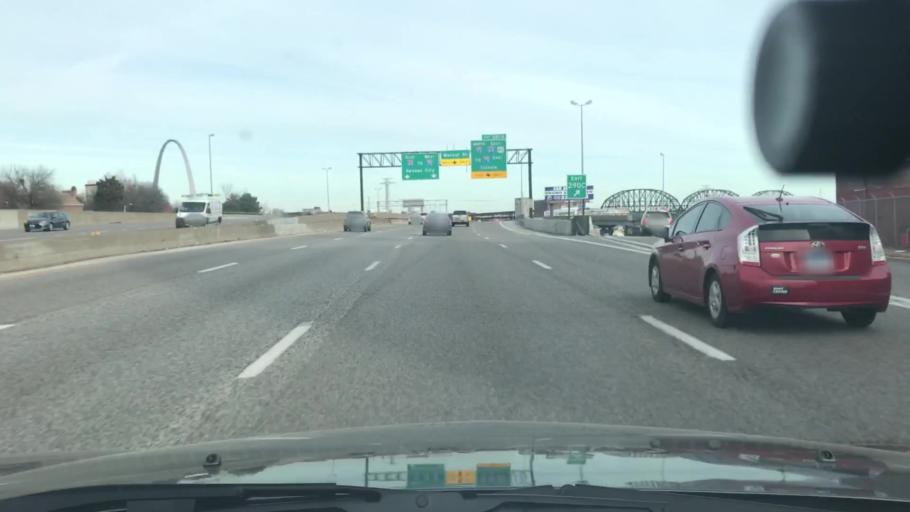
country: US
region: Missouri
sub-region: City of Saint Louis
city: St. Louis
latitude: 38.6125
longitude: -90.2008
